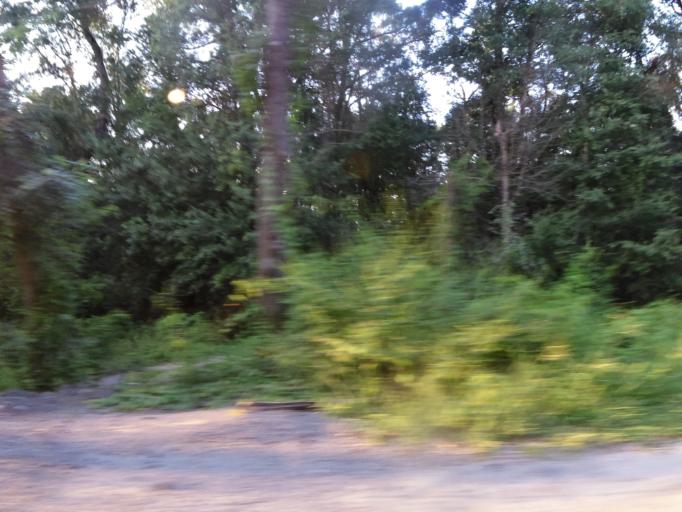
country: US
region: Florida
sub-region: Duval County
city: Baldwin
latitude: 30.3848
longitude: -82.0371
